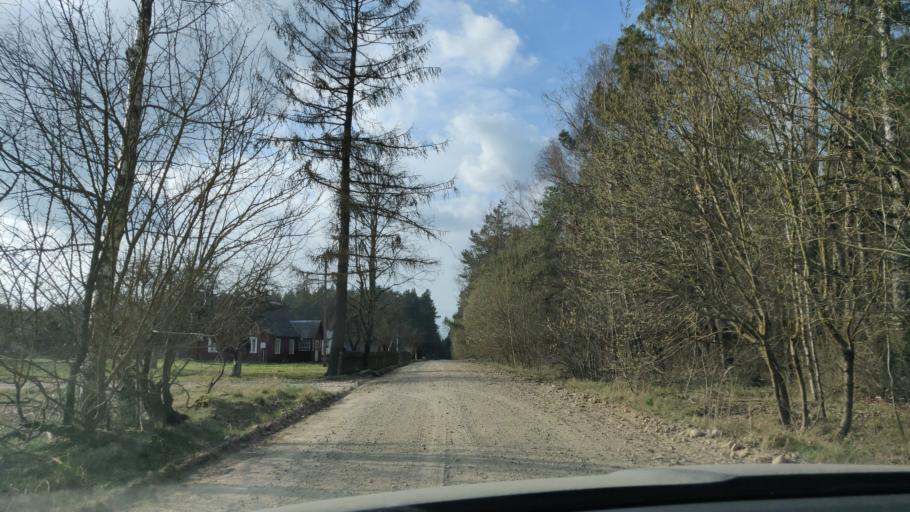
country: LT
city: Lentvaris
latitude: 54.5960
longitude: 25.0832
